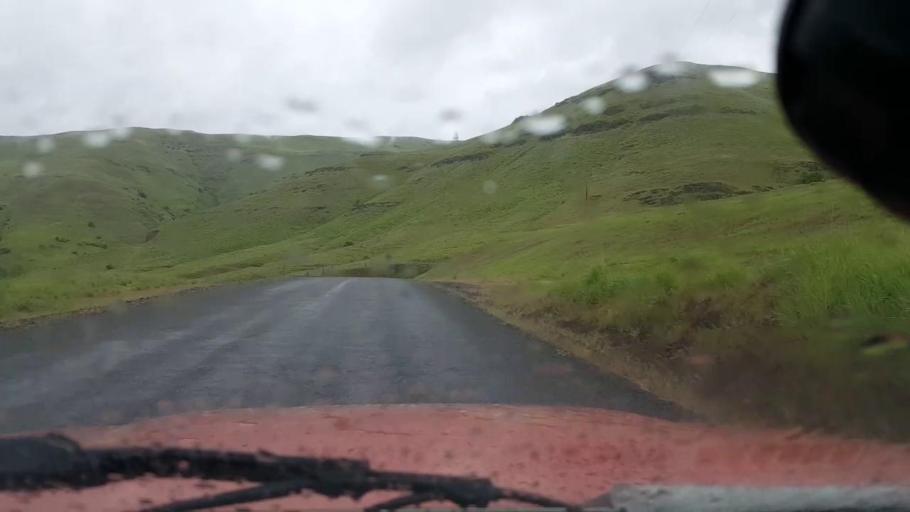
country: US
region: Washington
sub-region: Asotin County
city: Asotin
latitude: 46.0406
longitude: -117.2898
